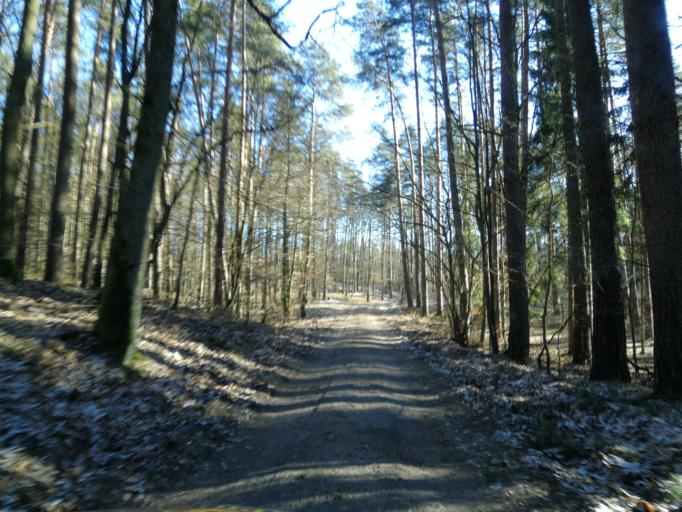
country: PL
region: Kujawsko-Pomorskie
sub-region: Powiat brodnicki
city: Gorzno
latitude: 53.2198
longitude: 19.7089
